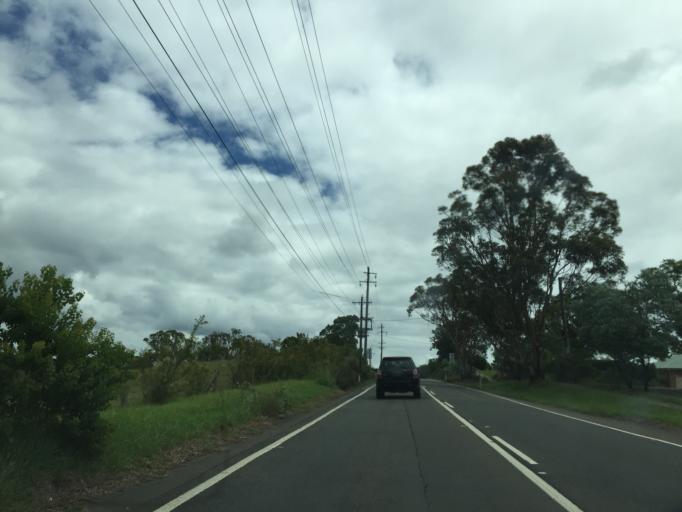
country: AU
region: New South Wales
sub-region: Hawkesbury
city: Richmond
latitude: -33.5656
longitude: 150.7038
